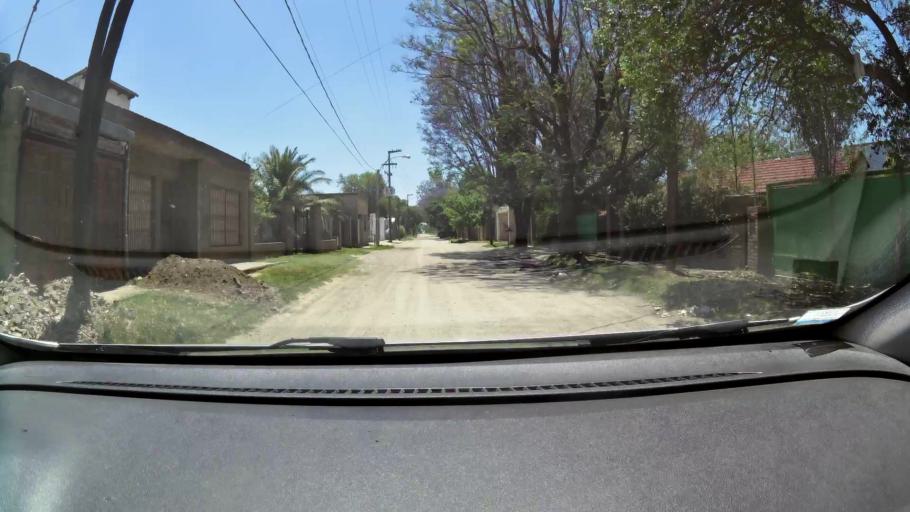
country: AR
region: Cordoba
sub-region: Departamento de Capital
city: Cordoba
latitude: -31.3822
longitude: -64.1282
